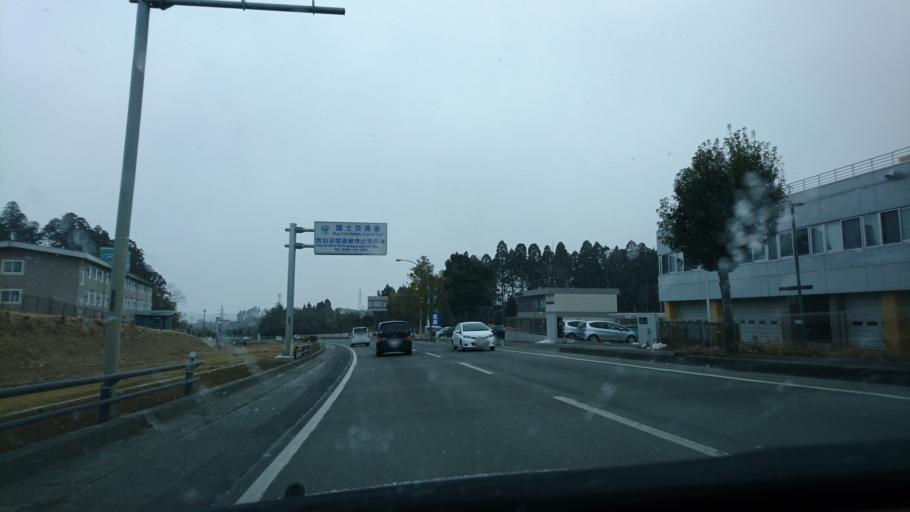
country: JP
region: Iwate
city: Ofunato
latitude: 38.8773
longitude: 141.5683
